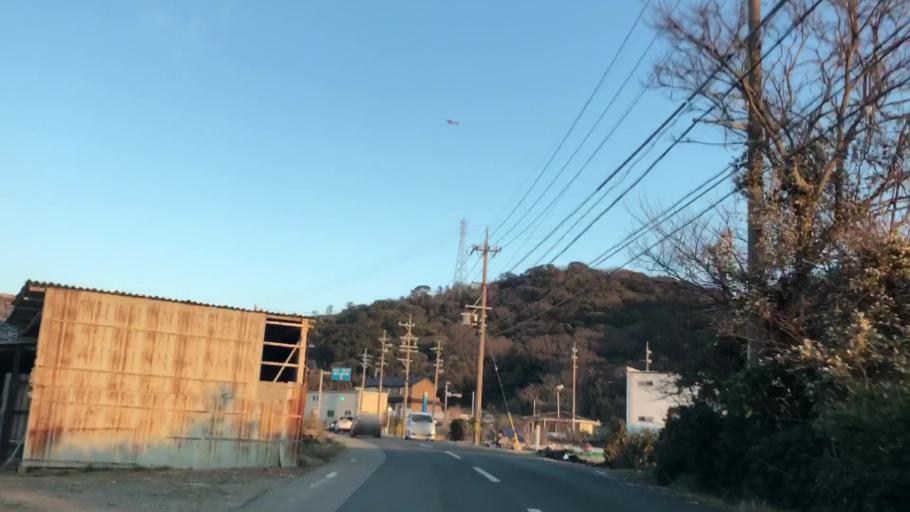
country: JP
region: Aichi
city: Toyohama
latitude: 34.6041
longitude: 137.0579
